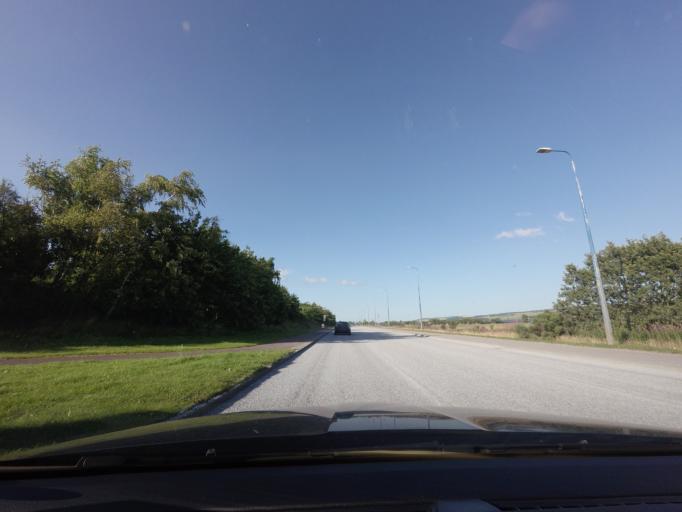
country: GB
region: Scotland
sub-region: Highland
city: Dingwall
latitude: 57.5848
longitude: -4.4306
